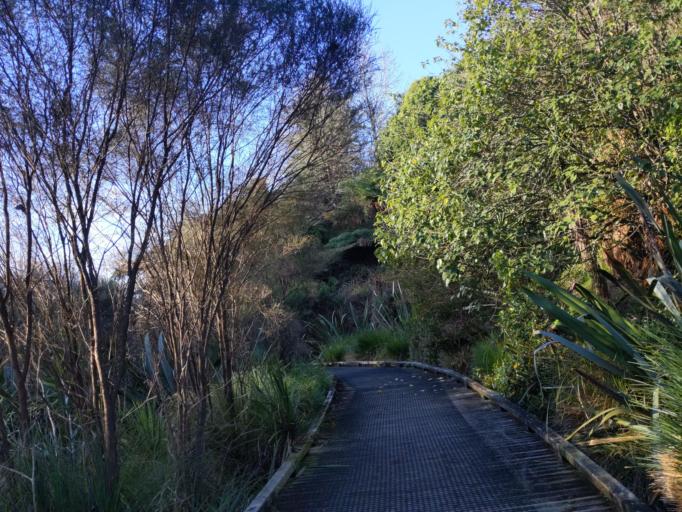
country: NZ
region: Waikato
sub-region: Hamilton City
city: Hamilton
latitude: -37.7401
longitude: 175.2755
